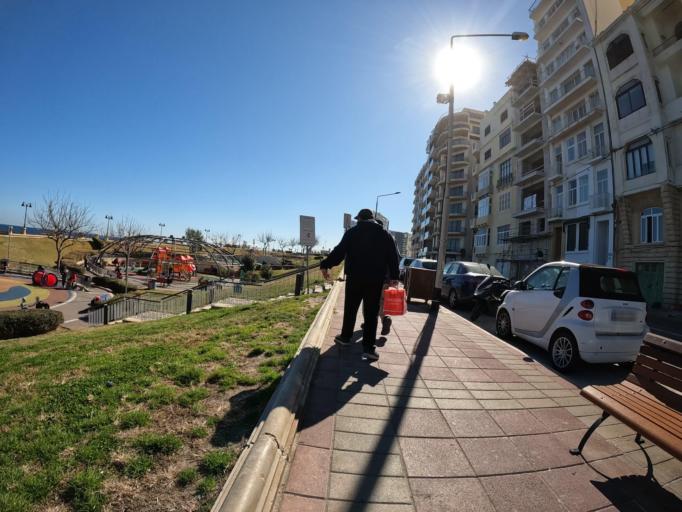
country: MT
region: Tas-Sliema
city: Sliema
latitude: 35.9105
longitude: 14.5092
